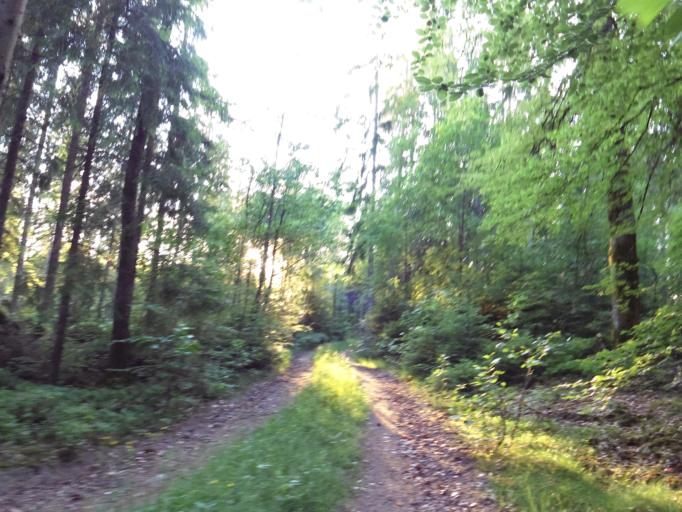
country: SE
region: Blekinge
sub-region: Olofstroms Kommun
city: Olofstroem
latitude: 56.4133
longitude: 14.5565
